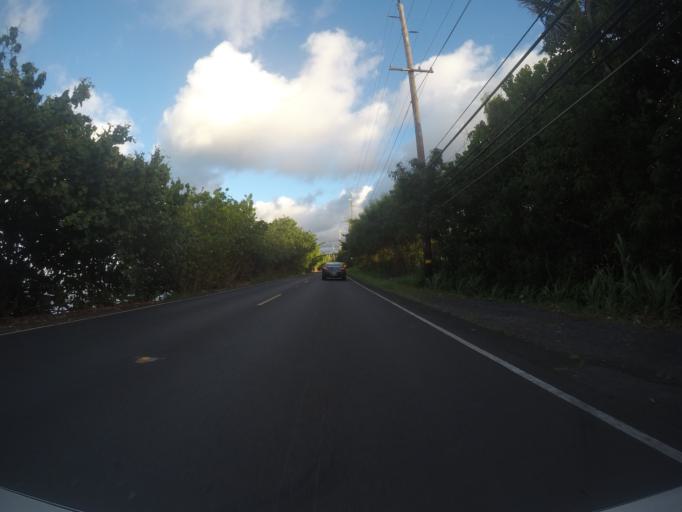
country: US
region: Hawaii
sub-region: Honolulu County
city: He'eia
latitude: 21.4473
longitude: -157.8141
